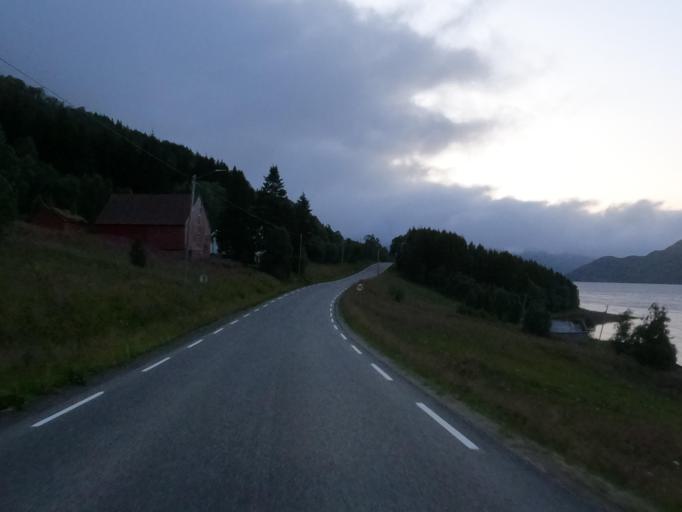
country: NO
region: Nordland
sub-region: Lodingen
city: Lodingen
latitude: 68.5857
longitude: 15.7913
